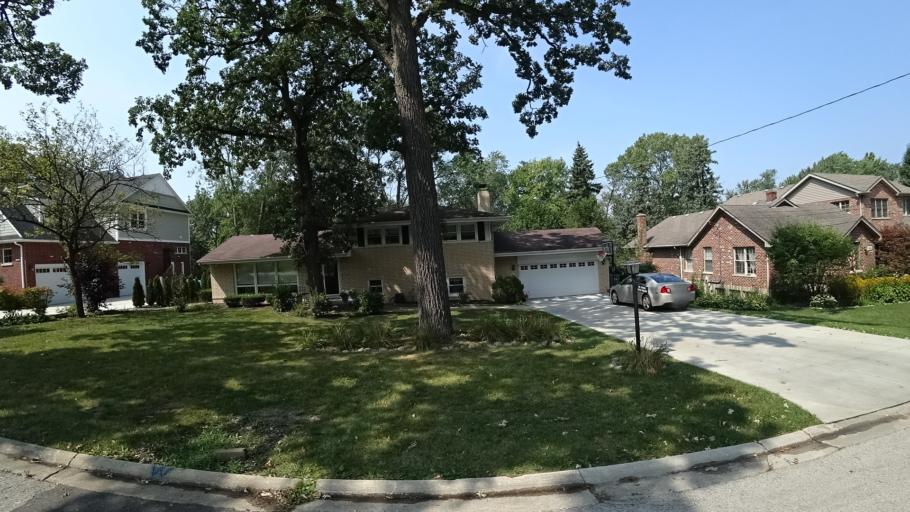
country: US
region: Illinois
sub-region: Cook County
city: Orland Park
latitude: 41.6237
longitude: -87.8657
